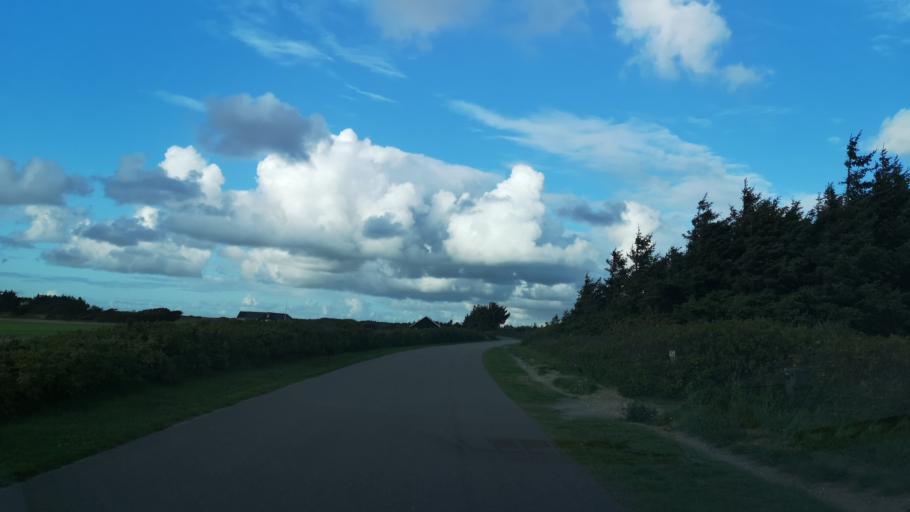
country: DK
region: Central Jutland
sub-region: Ringkobing-Skjern Kommune
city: Ringkobing
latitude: 56.1277
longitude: 8.1295
